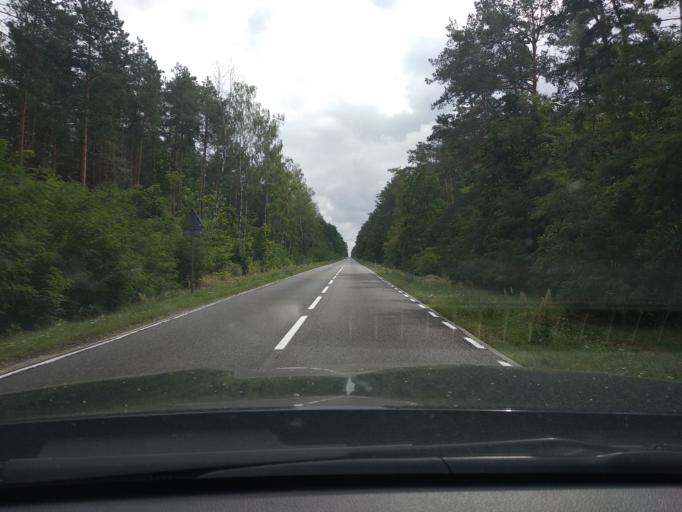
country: PL
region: Masovian Voivodeship
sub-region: Powiat pultuski
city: Obryte
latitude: 52.6452
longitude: 21.2583
